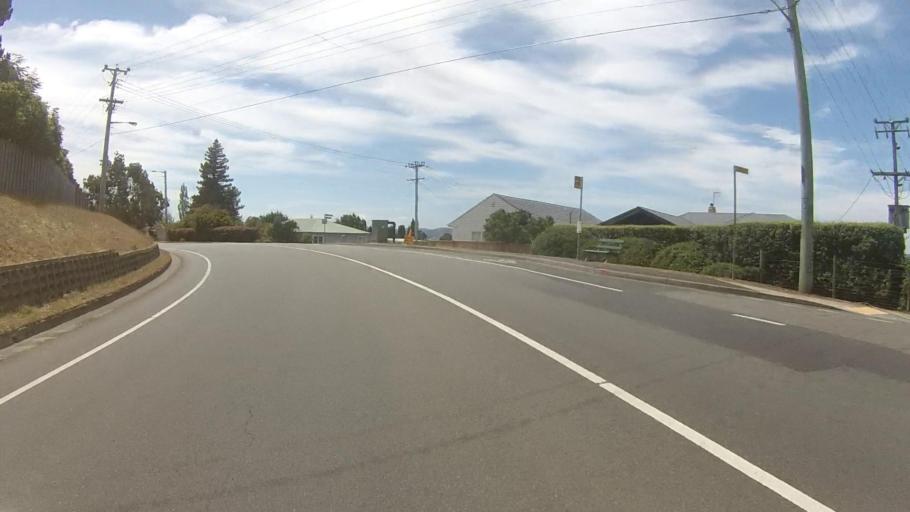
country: AU
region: Tasmania
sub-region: Kingborough
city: Taroona
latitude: -42.9366
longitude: 147.3540
